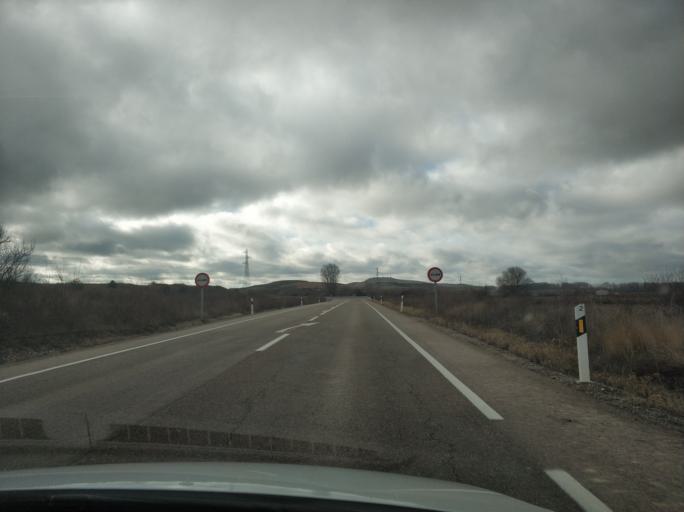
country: ES
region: Castille and Leon
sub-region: Provincia de Soria
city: San Esteban de Gormaz
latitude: 41.5664
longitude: -3.2401
